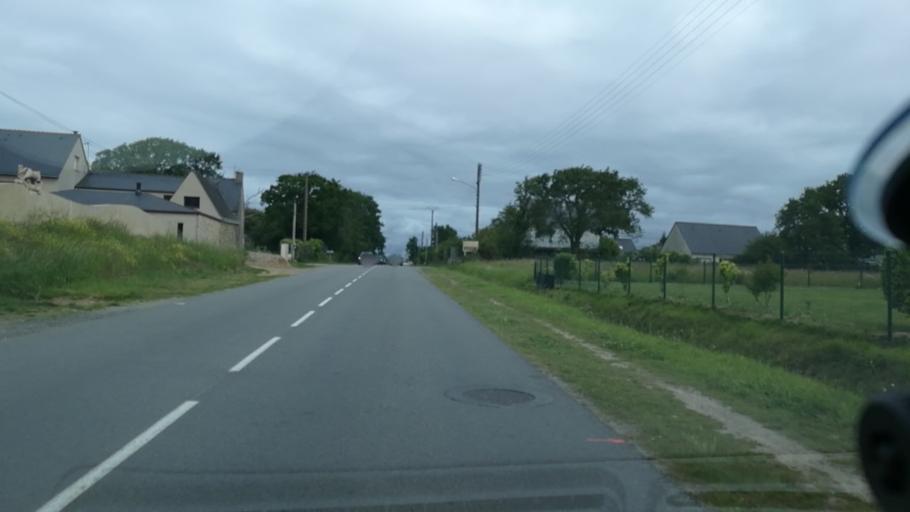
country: FR
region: Brittany
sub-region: Departement du Morbihan
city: Penestin
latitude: 47.4737
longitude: -2.4787
